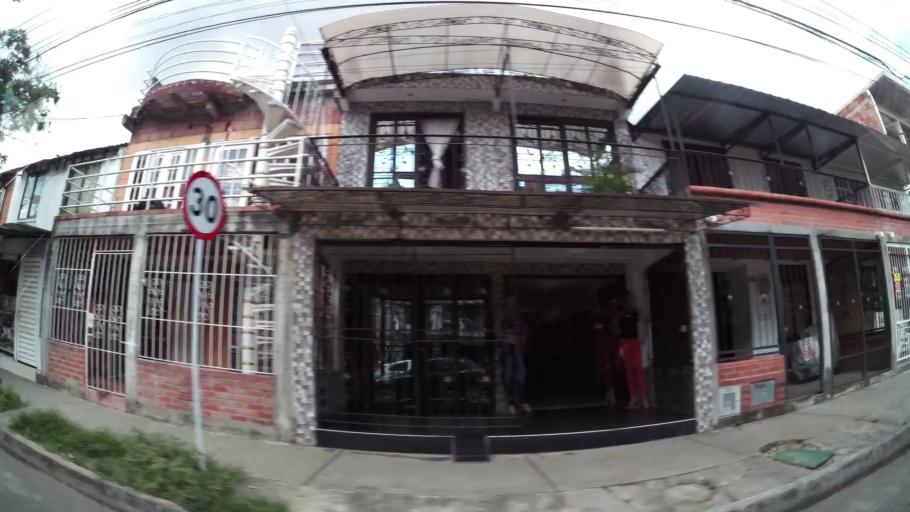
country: CO
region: Valle del Cauca
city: Cali
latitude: 3.3982
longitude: -76.5046
